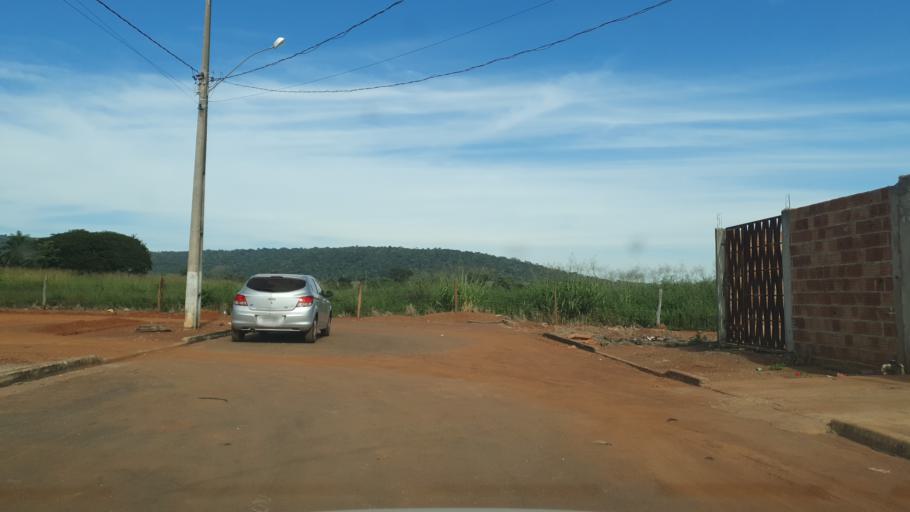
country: BR
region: Mato Grosso
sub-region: Pontes E Lacerda
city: Pontes e Lacerda
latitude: -15.2503
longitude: -59.3198
